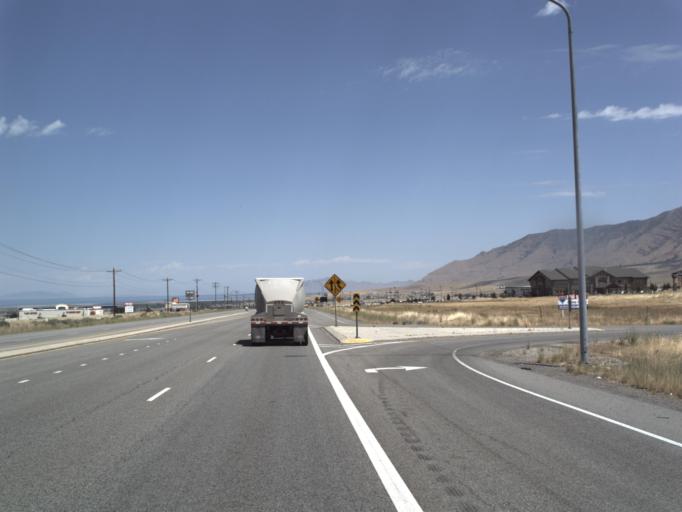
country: US
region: Utah
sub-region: Tooele County
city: Tooele
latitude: 40.5658
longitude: -112.2958
